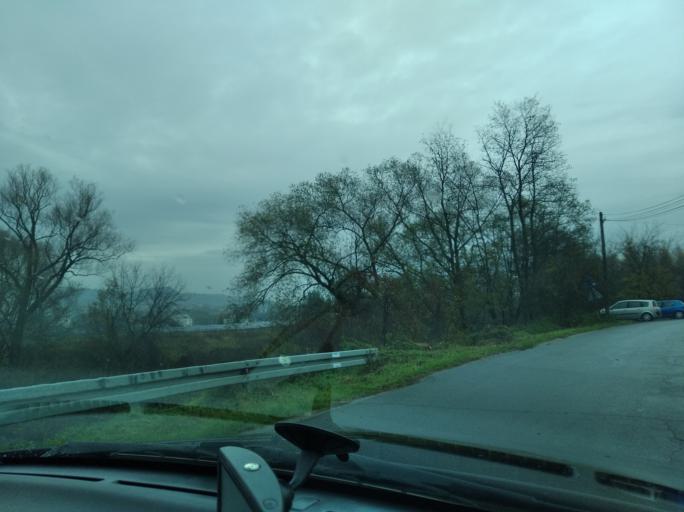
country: PL
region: Subcarpathian Voivodeship
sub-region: Powiat strzyzowski
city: Czudec
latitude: 49.9363
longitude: 21.8443
